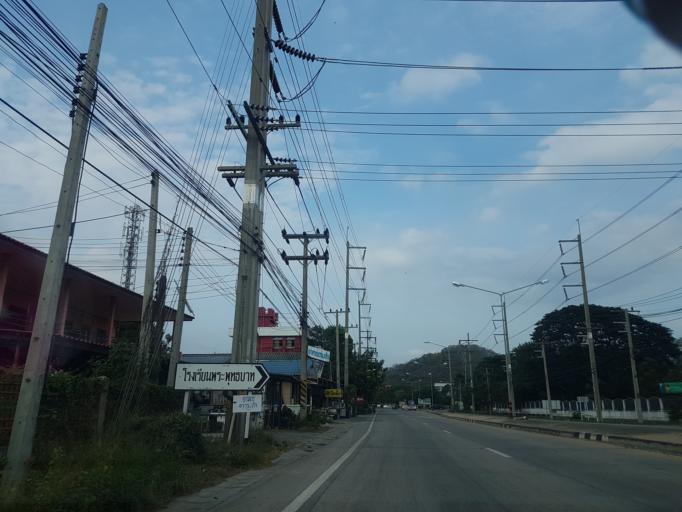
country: TH
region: Sara Buri
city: Phra Phutthabat
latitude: 14.7209
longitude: 100.8022
